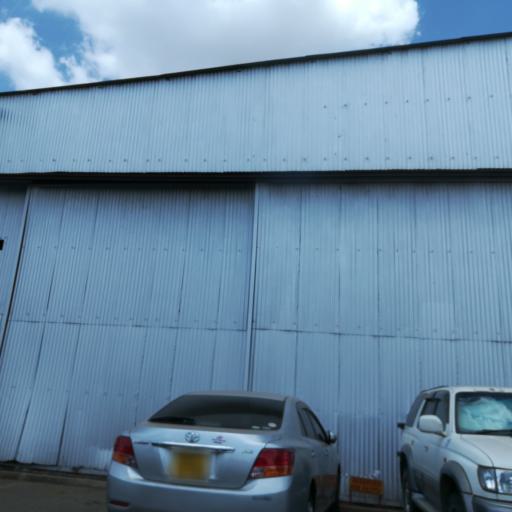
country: KE
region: Nairobi Area
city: Nairobi
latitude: -1.3182
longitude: 36.8126
